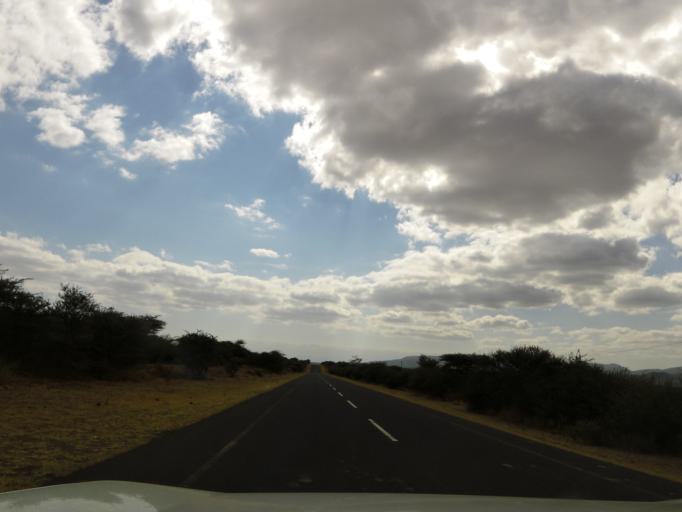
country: TZ
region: Arusha
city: Mto wa Mbu
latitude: -3.5399
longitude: 36.0850
